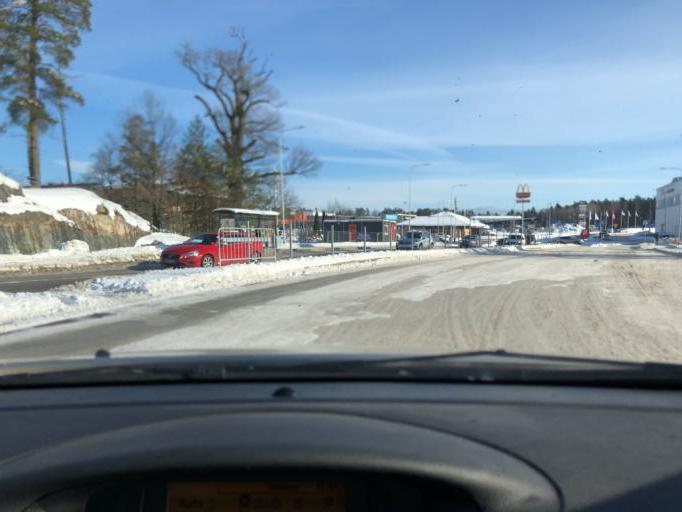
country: SE
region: Stockholm
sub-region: Varmdo Kommun
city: Mortnas
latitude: 59.3125
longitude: 18.4246
